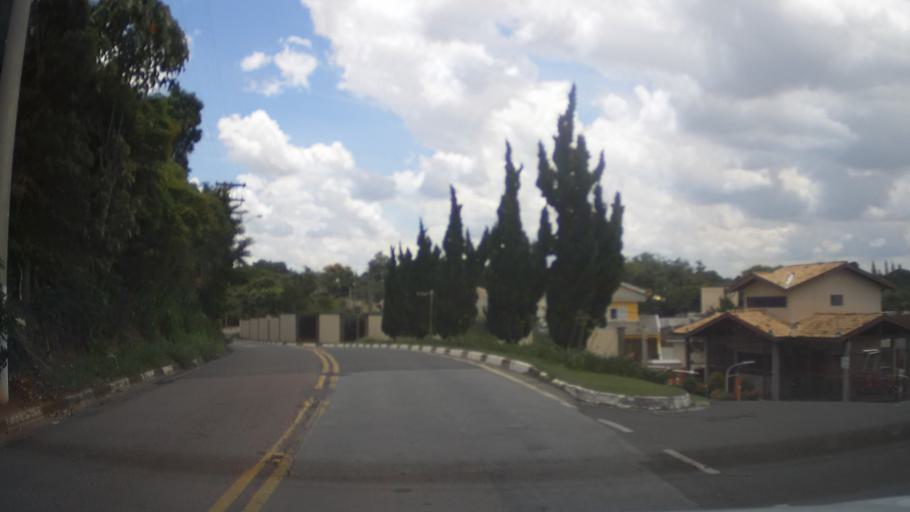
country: BR
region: Sao Paulo
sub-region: Vinhedo
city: Vinhedo
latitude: -23.0516
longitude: -46.9668
